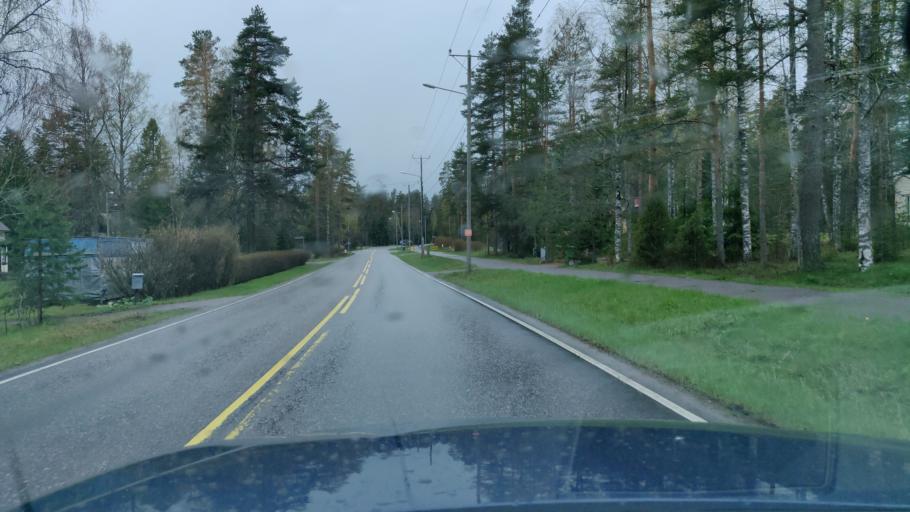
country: FI
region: Uusimaa
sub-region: Helsinki
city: Nurmijaervi
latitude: 60.5205
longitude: 24.7084
